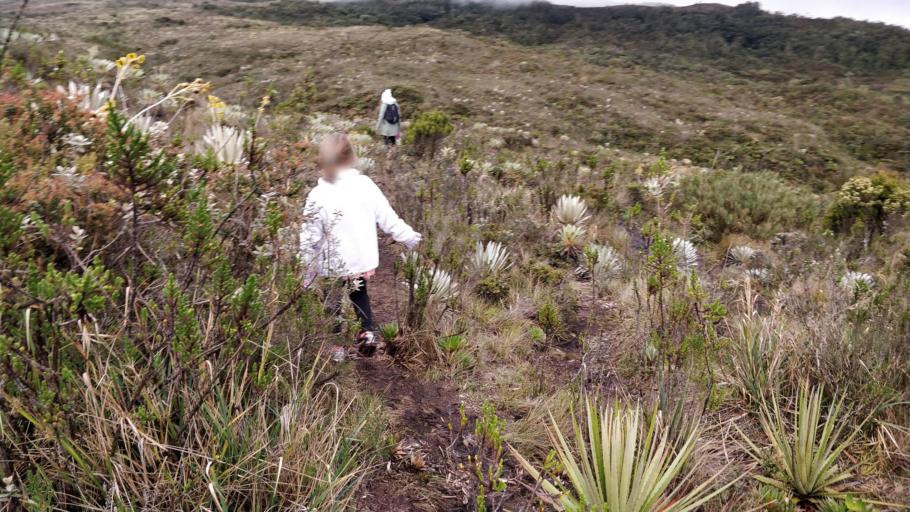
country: CO
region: Cundinamarca
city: Choachi
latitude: 4.5487
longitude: -73.9965
